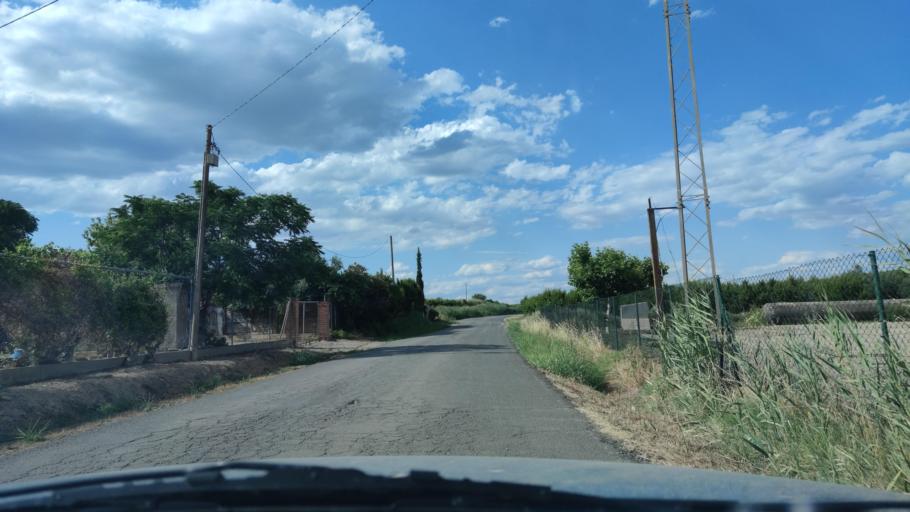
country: ES
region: Catalonia
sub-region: Provincia de Lleida
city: Alcarras
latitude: 41.5777
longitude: 0.5313
